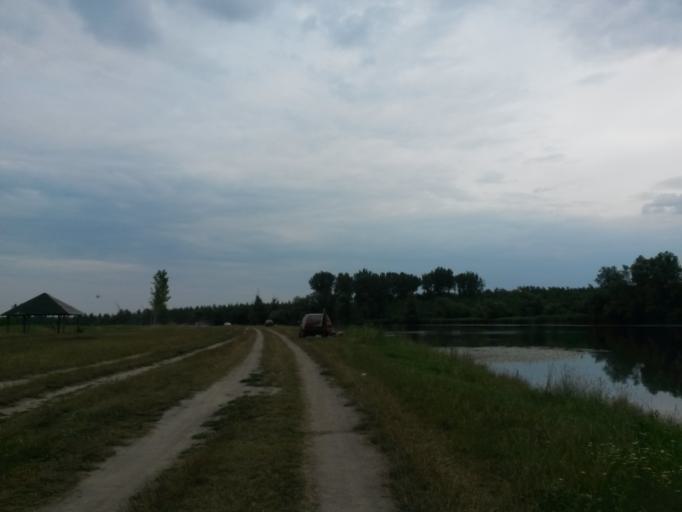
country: HR
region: Osjecko-Baranjska
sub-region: Grad Osijek
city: Bilje
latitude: 45.5880
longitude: 18.7435
